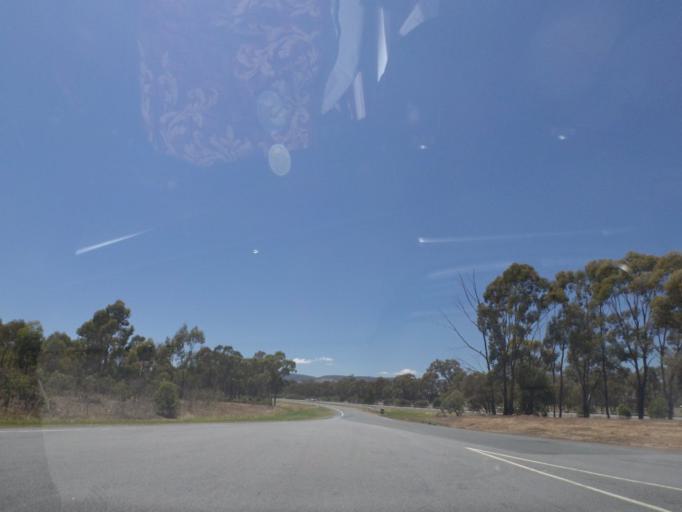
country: AU
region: Victoria
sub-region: Benalla
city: Benalla
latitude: -36.7136
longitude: 145.6361
